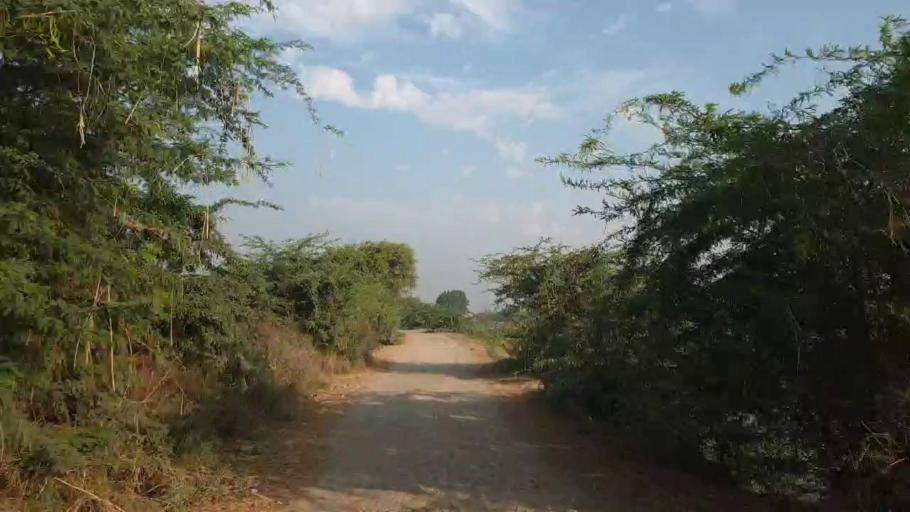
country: PK
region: Sindh
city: Tando Bago
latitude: 24.8020
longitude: 68.9593
